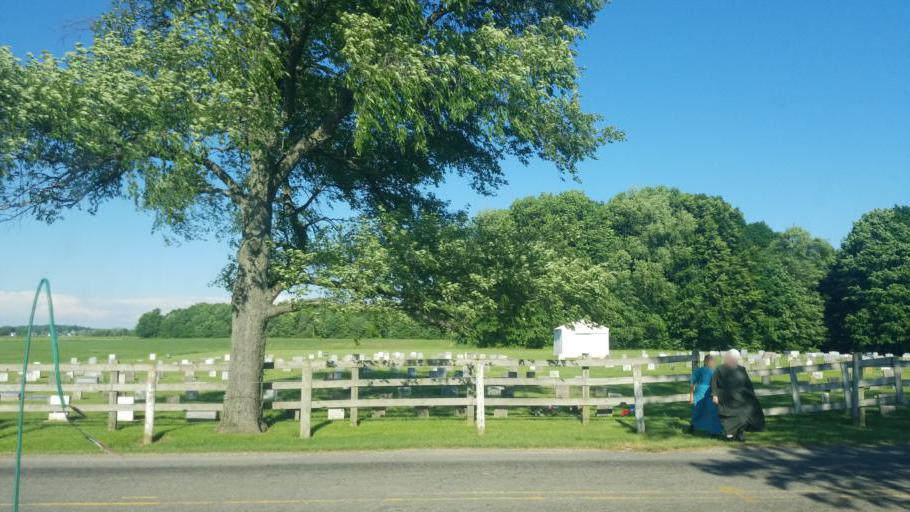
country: US
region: Indiana
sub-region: Elkhart County
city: Nappanee
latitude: 41.4501
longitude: -86.0497
